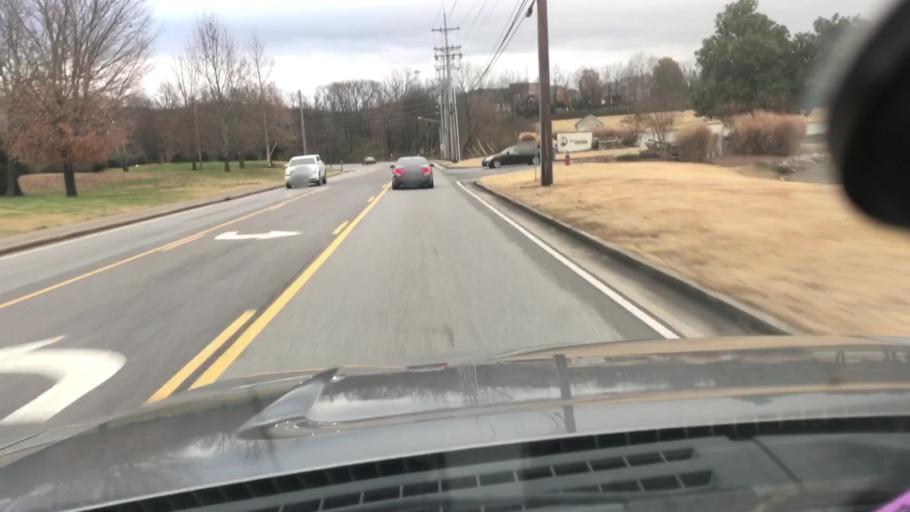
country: US
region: Tennessee
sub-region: Williamson County
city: Brentwood Estates
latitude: 35.9642
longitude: -86.7860
